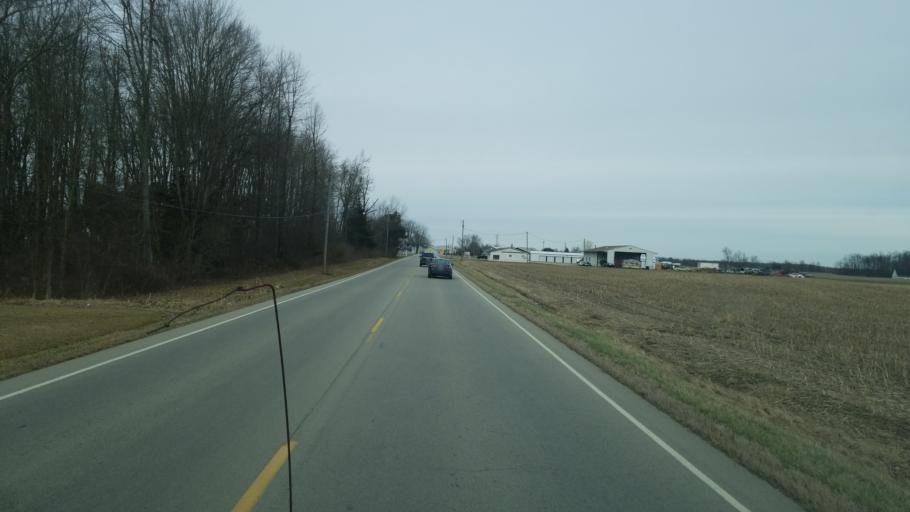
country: US
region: Ohio
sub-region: Adams County
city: Winchester
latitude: 39.0597
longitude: -83.7036
